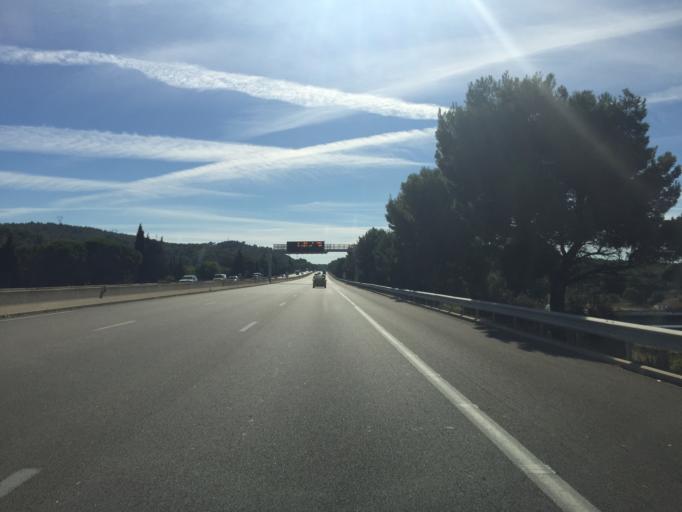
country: FR
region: Provence-Alpes-Cote d'Azur
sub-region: Departement des Bouches-du-Rhone
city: Salon-de-Provence
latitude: 43.6591
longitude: 5.1021
